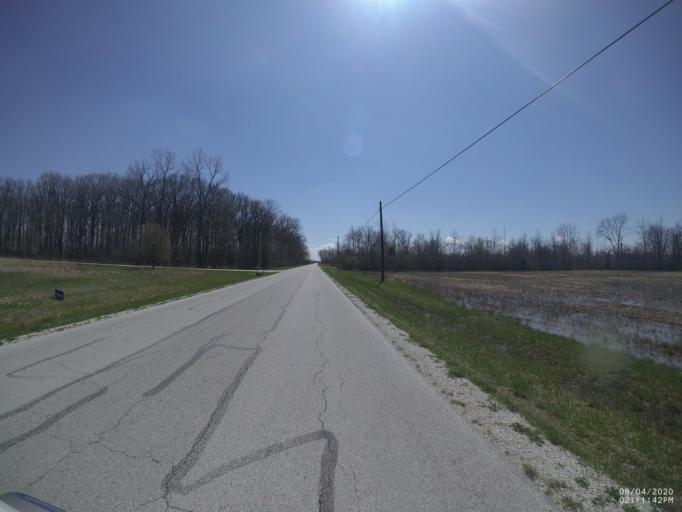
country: US
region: Ohio
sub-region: Sandusky County
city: Gibsonburg
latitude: 41.2613
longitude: -83.2645
